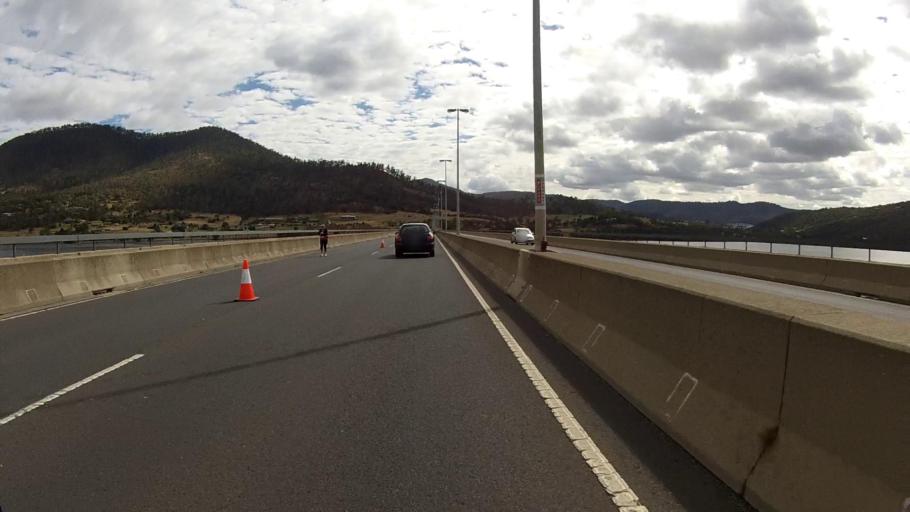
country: AU
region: Tasmania
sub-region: Glenorchy
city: Goodwood
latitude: -42.8197
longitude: 147.3046
